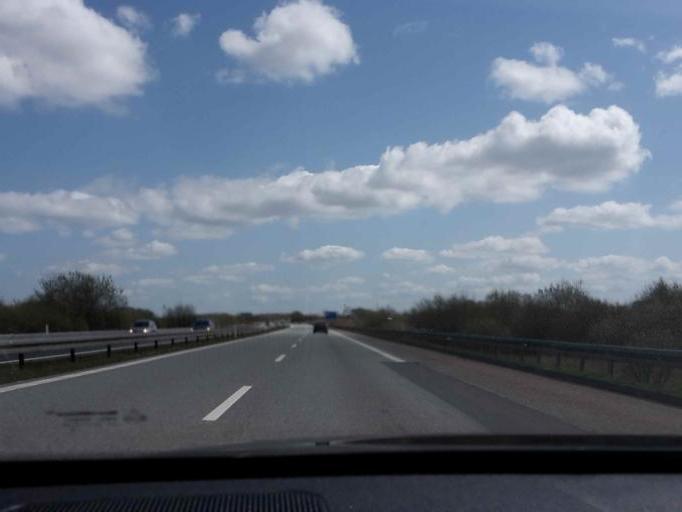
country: DK
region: South Denmark
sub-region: Vejen Kommune
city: Brorup
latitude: 55.5072
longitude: 9.0021
